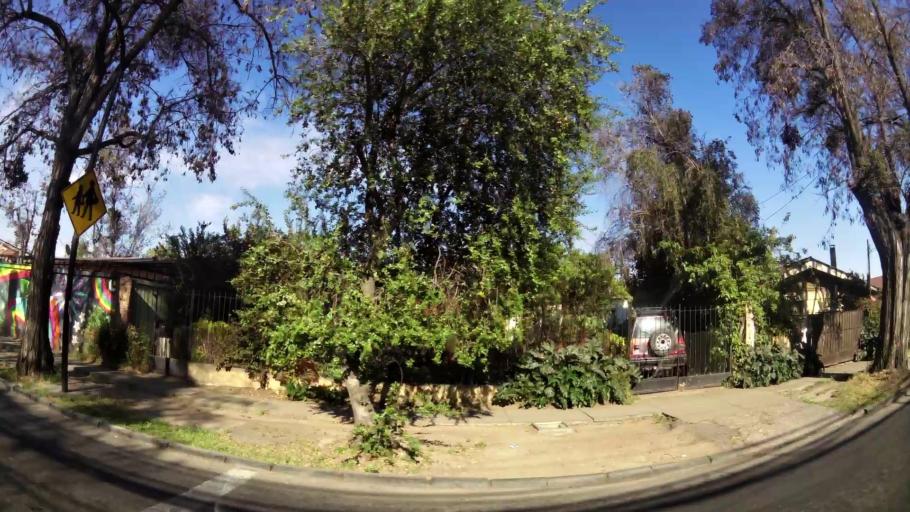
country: CL
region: Santiago Metropolitan
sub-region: Provincia de Santiago
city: Villa Presidente Frei, Nunoa, Santiago, Chile
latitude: -33.4443
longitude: -70.5523
